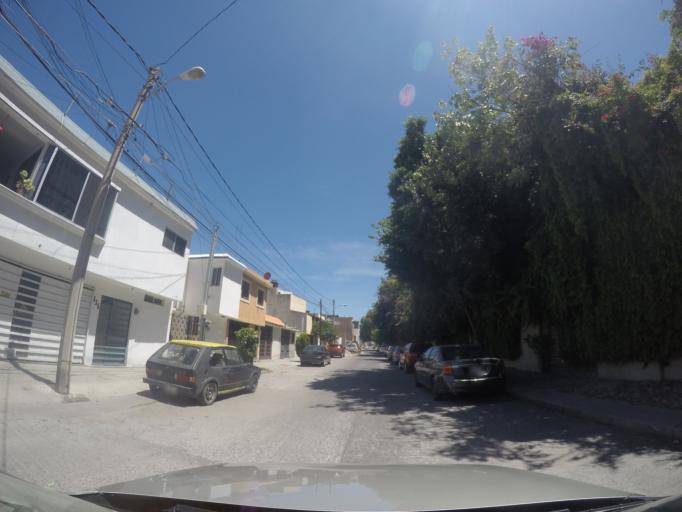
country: MX
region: San Luis Potosi
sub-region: San Luis Potosi
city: San Luis Potosi
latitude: 22.1580
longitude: -100.9942
